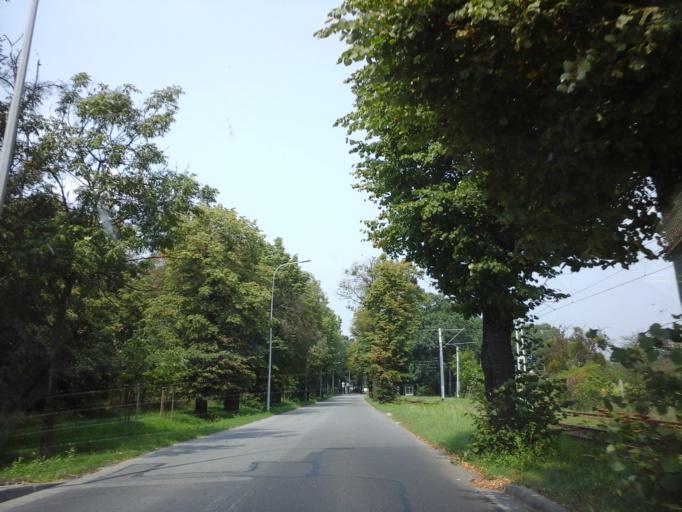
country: PL
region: Lower Silesian Voivodeship
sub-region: Powiat wroclawski
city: Wroclaw
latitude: 51.1364
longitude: 16.9960
